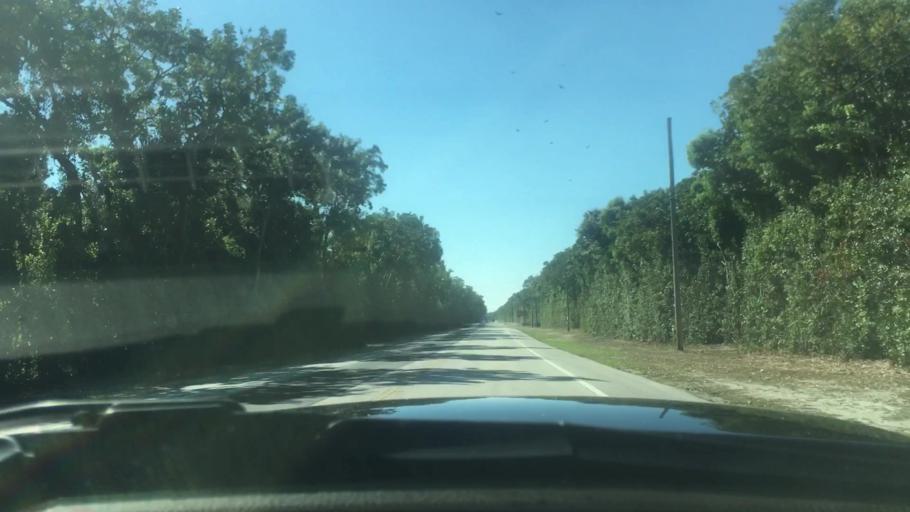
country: US
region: Florida
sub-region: Monroe County
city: North Key Largo
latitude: 25.2379
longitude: -80.3235
